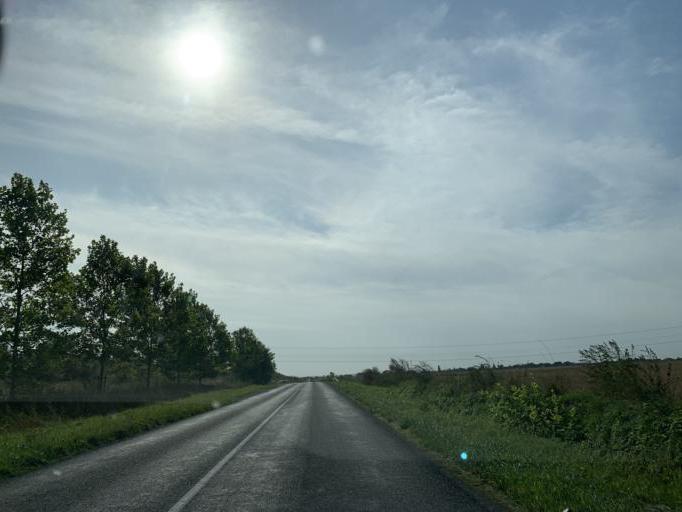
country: FR
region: Ile-de-France
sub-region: Departement de Seine-et-Marne
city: Claye-Souilly
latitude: 48.9386
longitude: 2.7002
